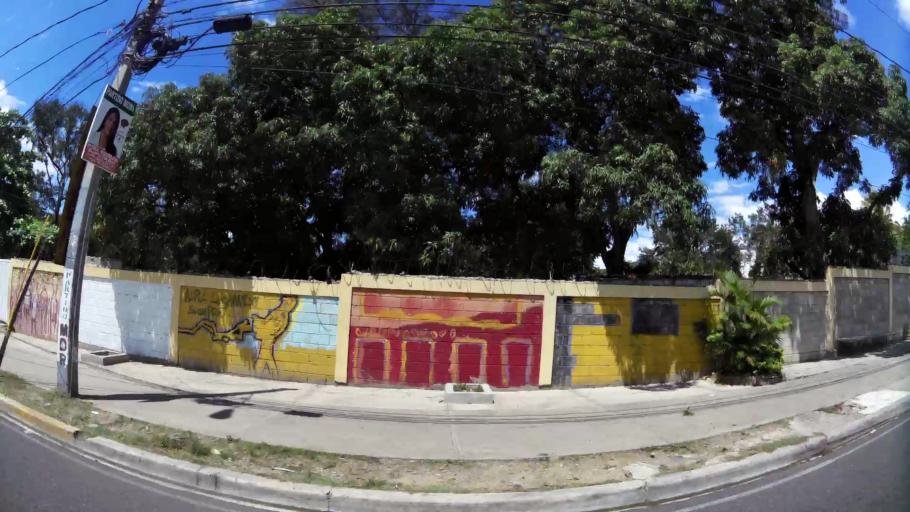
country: DO
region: Santiago
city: Santiago de los Caballeros
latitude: 19.4626
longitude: -70.6772
